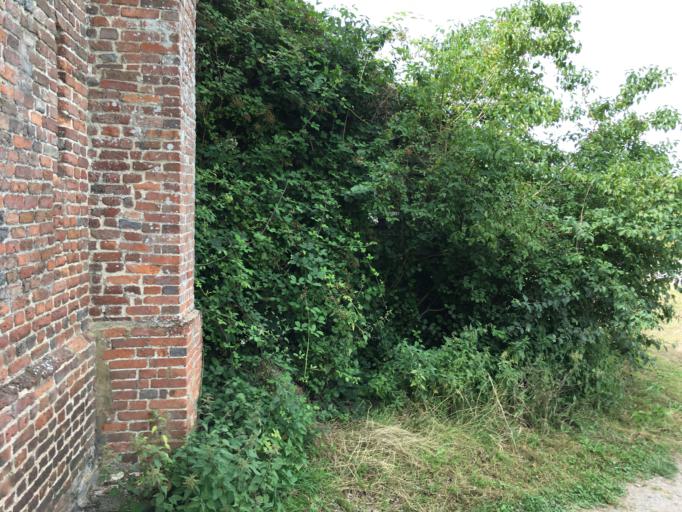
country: GB
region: England
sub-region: Kent
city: Cranbrook
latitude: 51.1164
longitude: 0.5815
